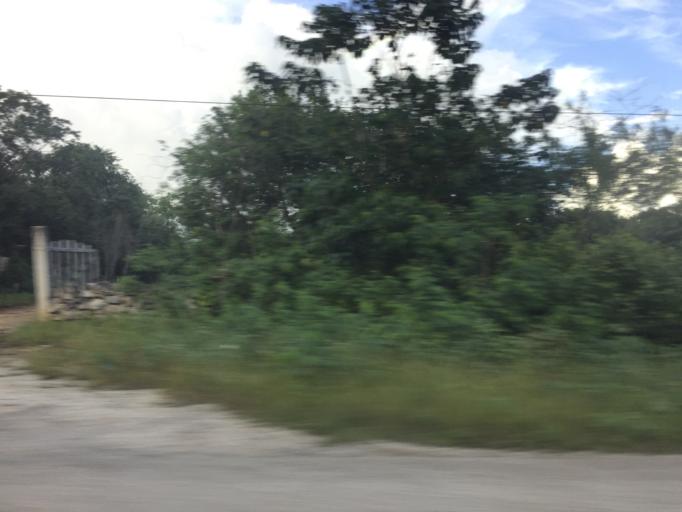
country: MX
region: Quintana Roo
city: Tulum
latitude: 20.2904
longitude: -87.5071
